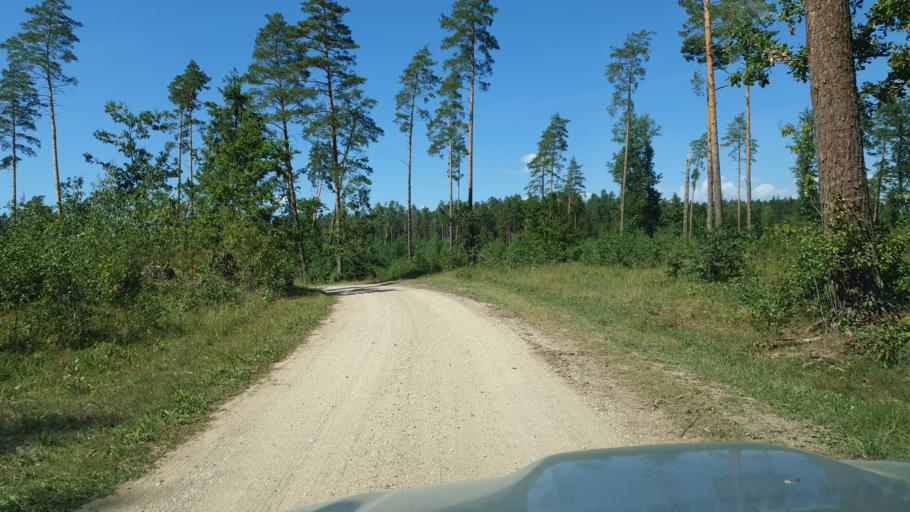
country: LT
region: Vilnius County
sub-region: Vilniaus Rajonas
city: Vievis
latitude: 54.9010
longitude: 24.8858
